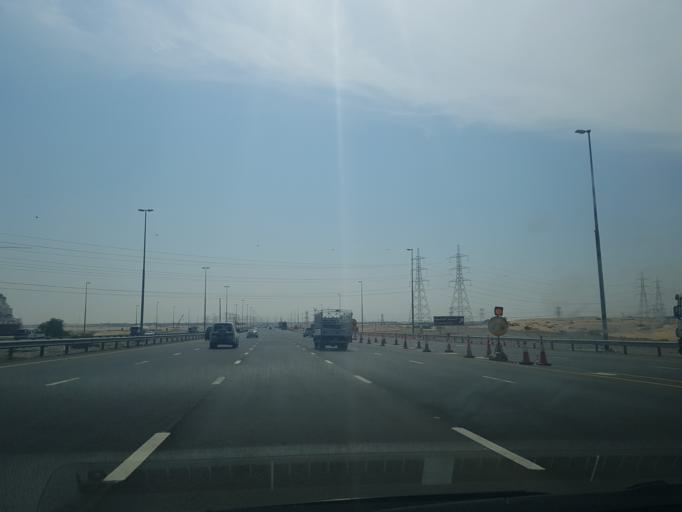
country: AE
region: Ash Shariqah
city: Sharjah
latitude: 25.2467
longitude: 55.5699
